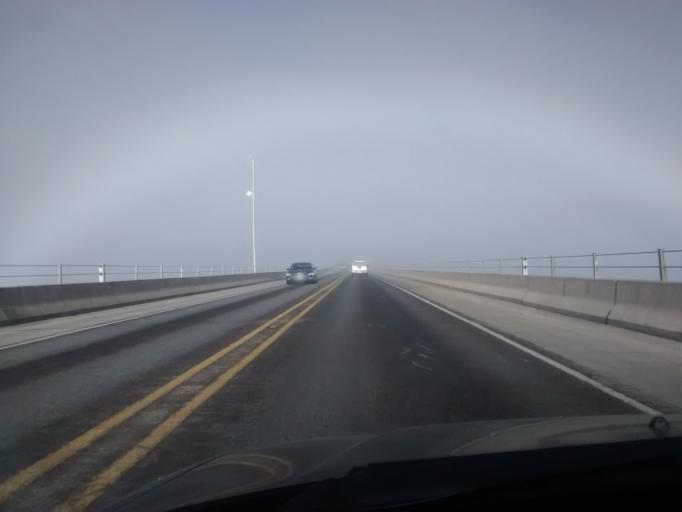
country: US
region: Washington
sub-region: Kitsap County
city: Lofall
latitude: 47.8630
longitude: -122.6300
